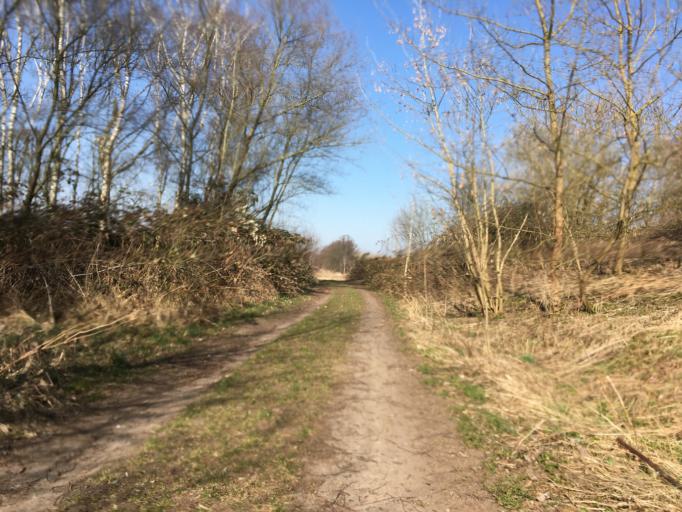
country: DE
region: Berlin
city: Buch
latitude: 52.6654
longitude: 13.4491
